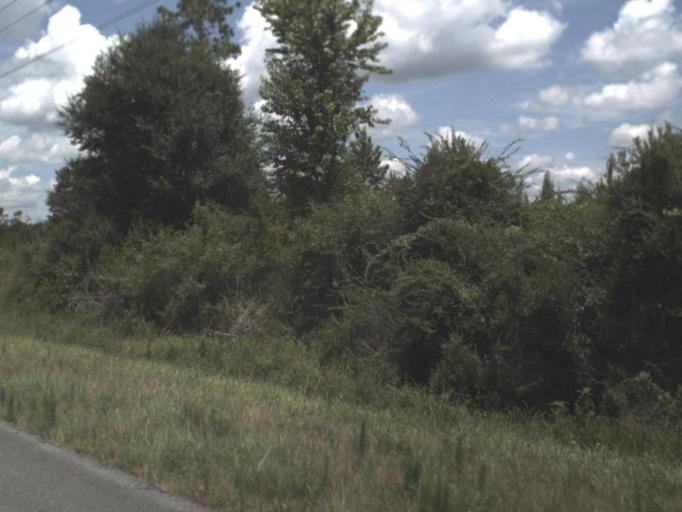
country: US
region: Florida
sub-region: Taylor County
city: Perry
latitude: 30.0940
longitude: -83.6844
